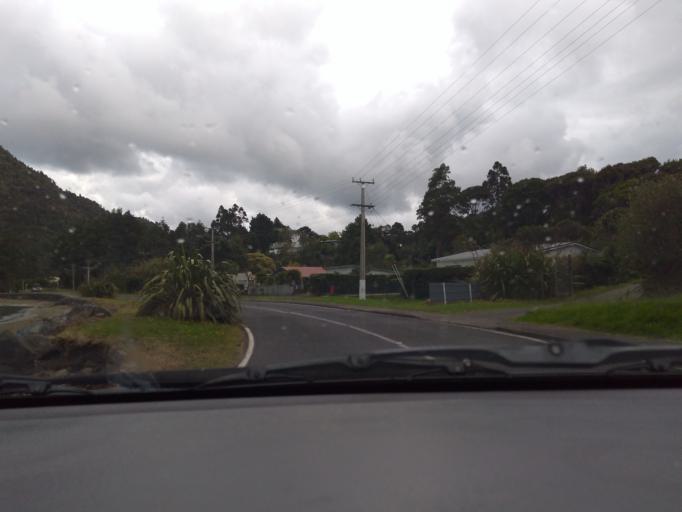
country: NZ
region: Auckland
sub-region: Auckland
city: Titirangi
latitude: -37.0005
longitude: 174.5723
